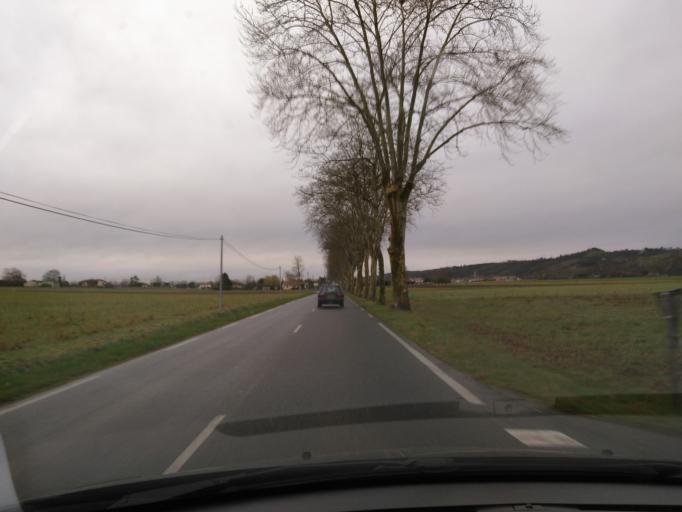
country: FR
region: Midi-Pyrenees
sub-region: Departement de la Haute-Garonne
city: Montesquieu-Volvestre
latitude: 43.1918
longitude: 1.2359
